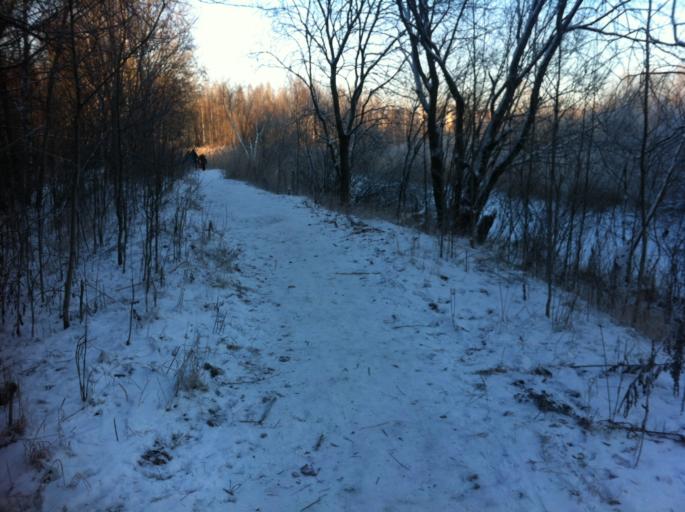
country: RU
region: St.-Petersburg
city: Uritsk
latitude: 59.8546
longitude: 30.1622
